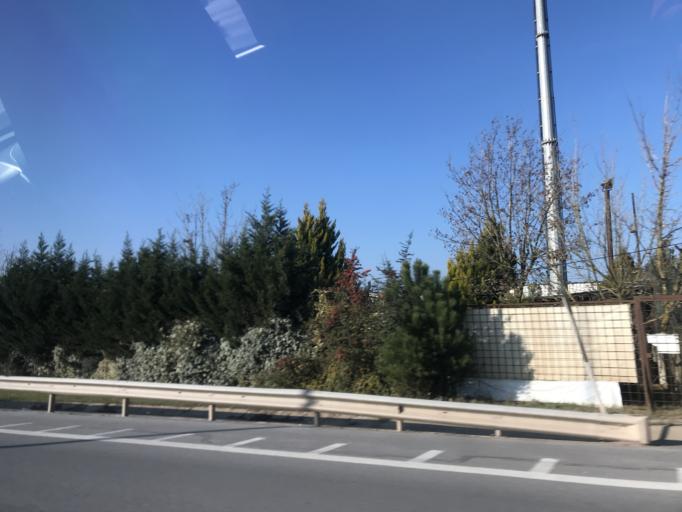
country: TR
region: Istanbul
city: Sultanbeyli
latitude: 40.9350
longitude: 29.3595
